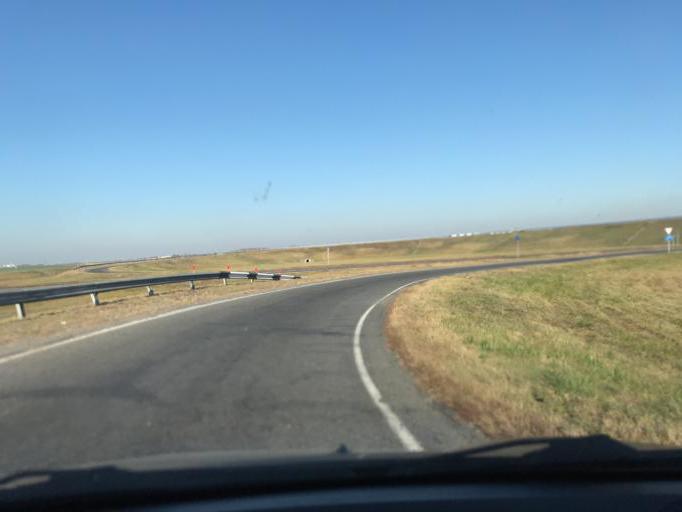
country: BY
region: Gomel
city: Horad Rechytsa
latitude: 52.2906
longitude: 30.4639
